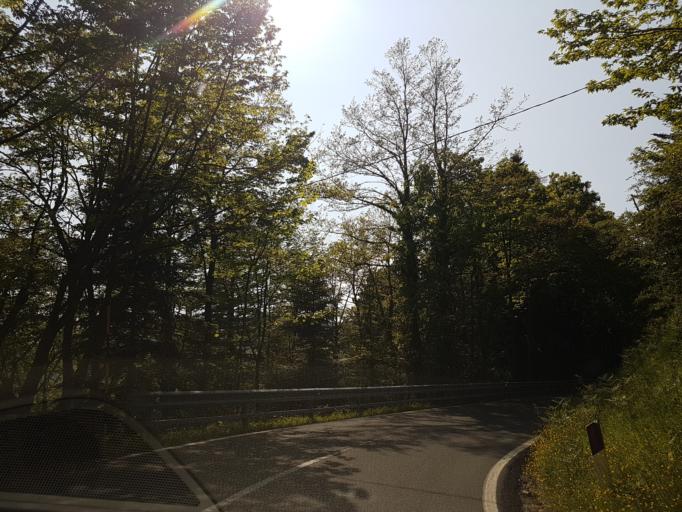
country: IT
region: Tuscany
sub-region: Province of Arezzo
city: Chiusi della Verna
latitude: 43.7937
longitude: 11.8934
